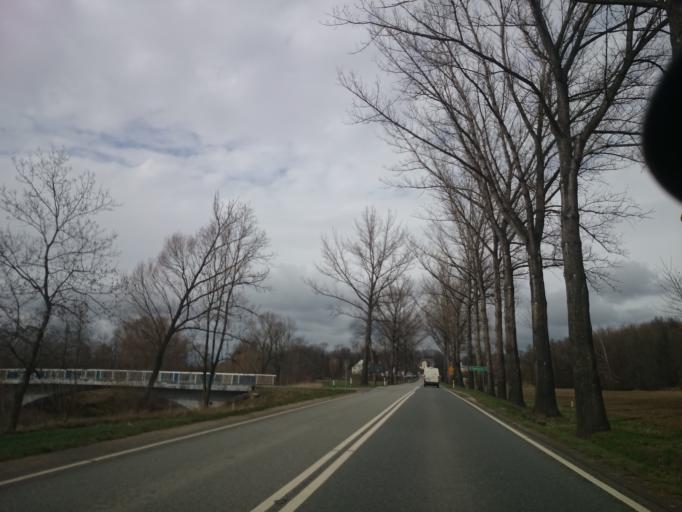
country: PL
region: Lower Silesian Voivodeship
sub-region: Powiat klodzki
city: Bystrzyca Klodzka
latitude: 50.3178
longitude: 16.6606
